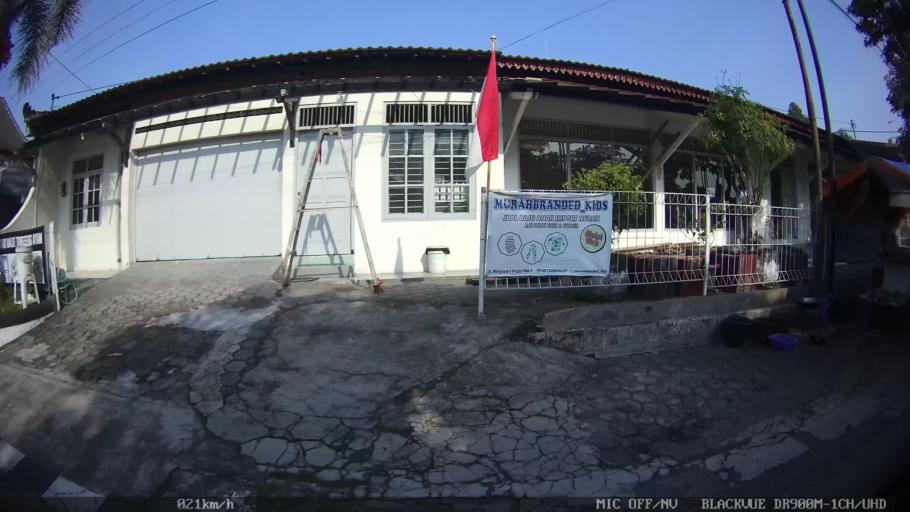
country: ID
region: Daerah Istimewa Yogyakarta
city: Yogyakarta
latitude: -7.8107
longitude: 110.3577
